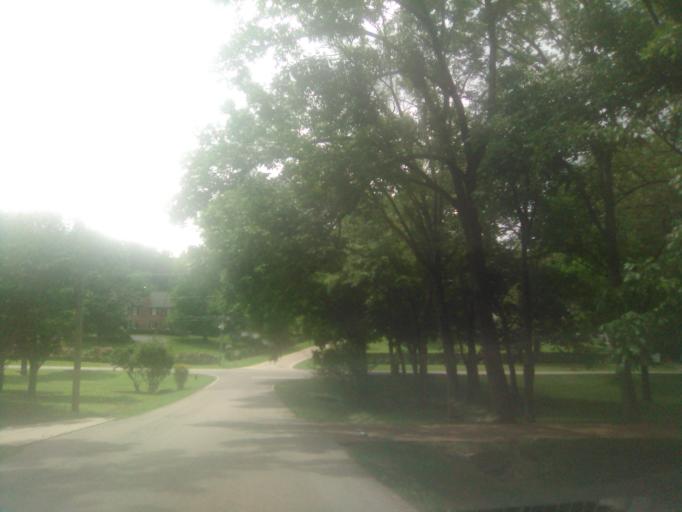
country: US
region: Tennessee
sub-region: Davidson County
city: Belle Meade
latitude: 36.1011
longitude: -86.8448
